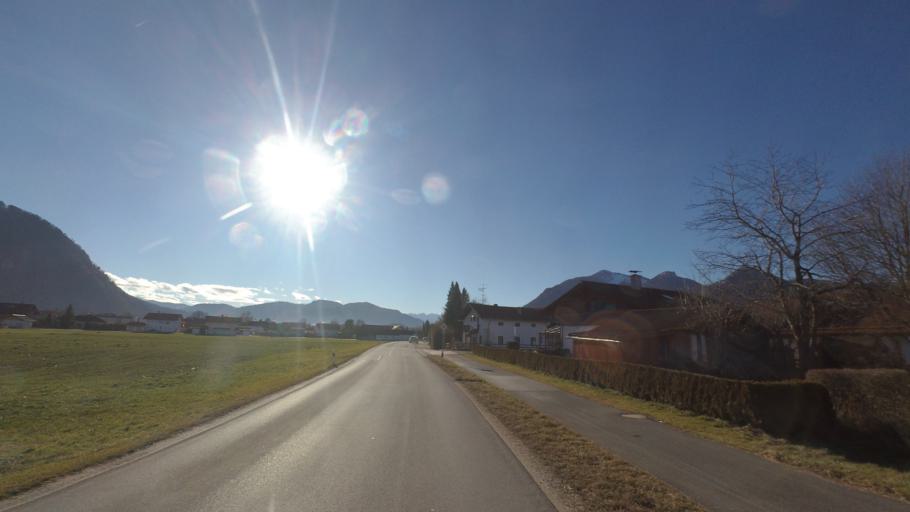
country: DE
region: Bavaria
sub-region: Upper Bavaria
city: Grassau
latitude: 47.7876
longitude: 12.4676
